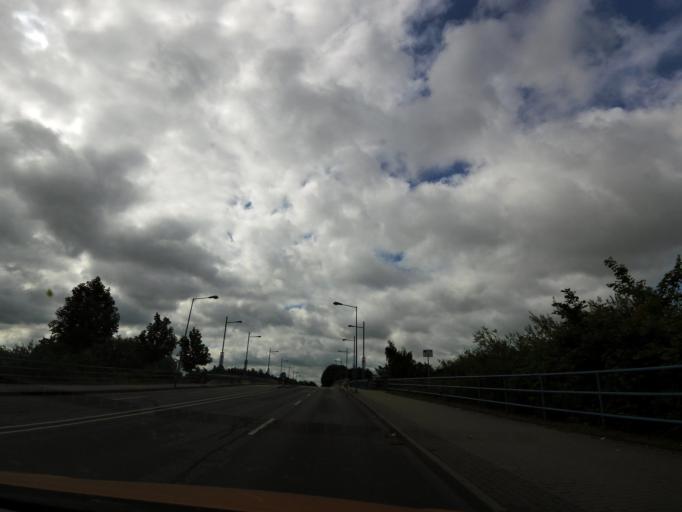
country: DE
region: Mecklenburg-Vorpommern
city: Guestrow
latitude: 53.7977
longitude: 12.1822
